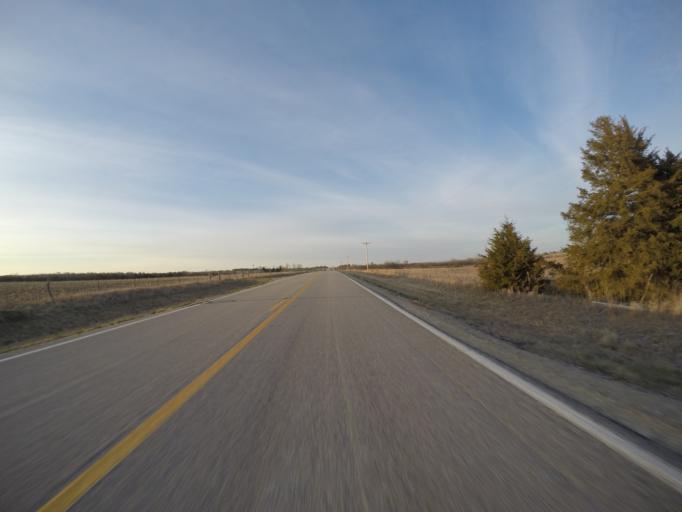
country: US
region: Kansas
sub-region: Clay County
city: Clay Center
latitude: 39.4164
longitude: -96.8488
